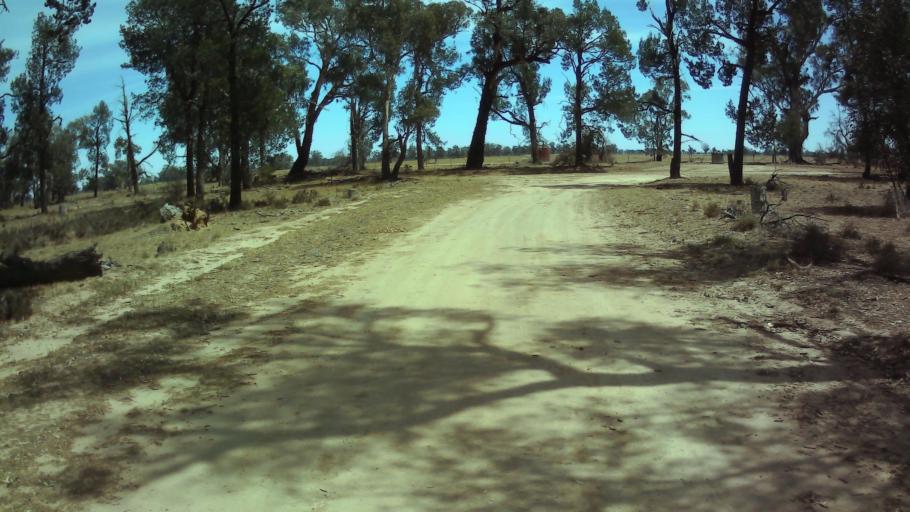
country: AU
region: New South Wales
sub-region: Weddin
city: Grenfell
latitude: -34.0322
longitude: 147.9330
